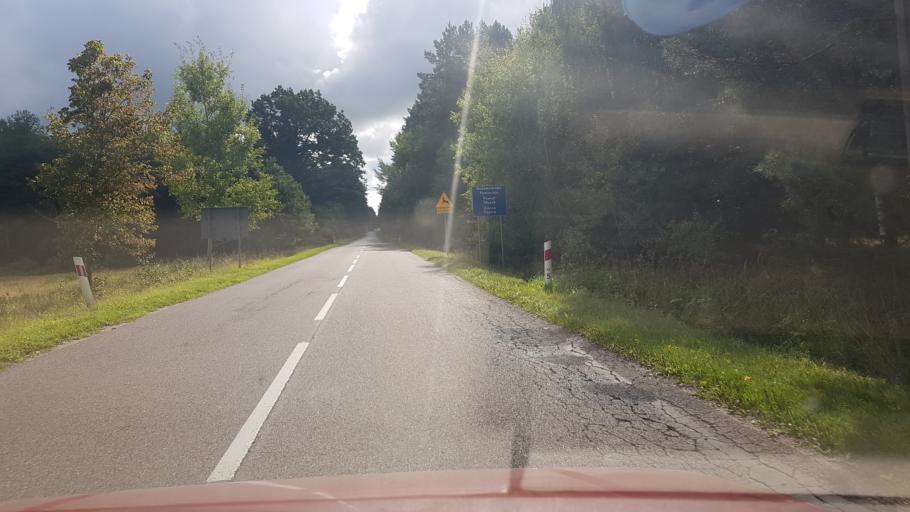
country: PL
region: West Pomeranian Voivodeship
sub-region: Powiat koszalinski
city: Polanow
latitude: 54.1055
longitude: 16.7976
